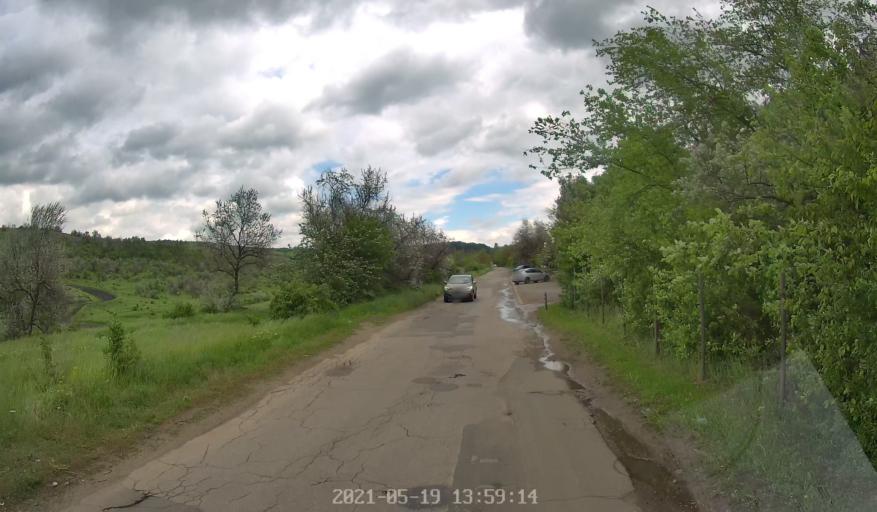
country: MD
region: Chisinau
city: Chisinau
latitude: 47.0413
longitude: 28.9222
